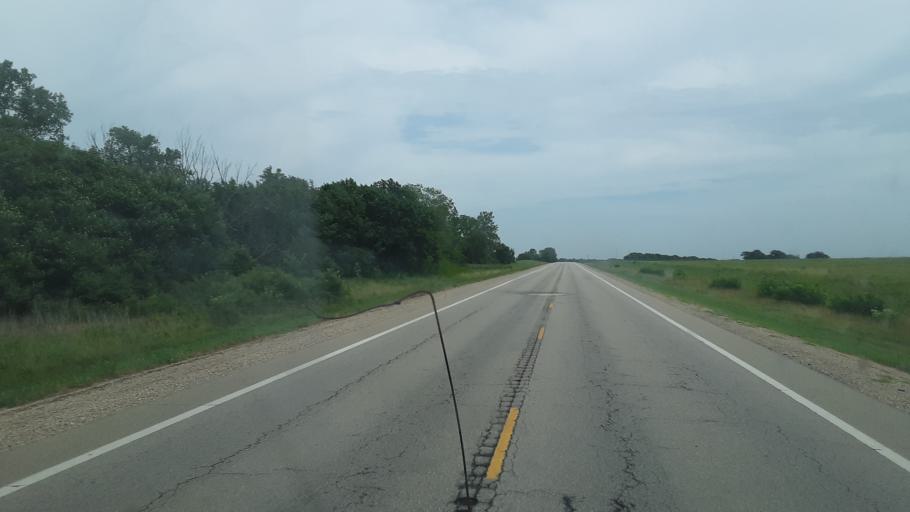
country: US
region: Kansas
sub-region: Woodson County
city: Yates Center
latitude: 37.8729
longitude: -95.7840
